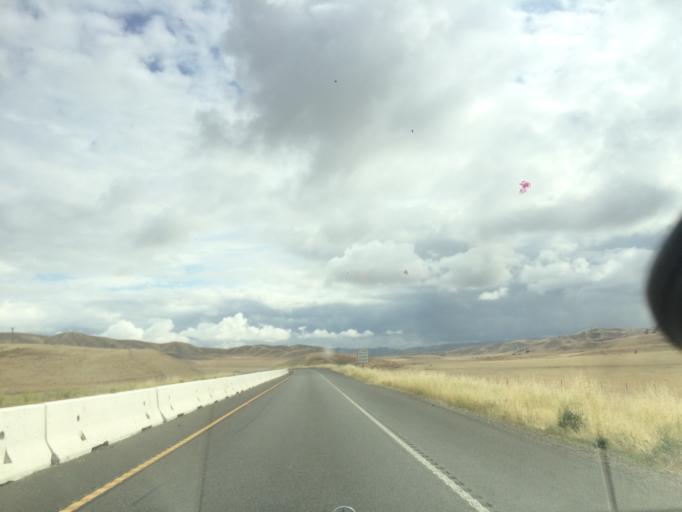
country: US
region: California
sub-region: San Luis Obispo County
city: Shandon
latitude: 35.6987
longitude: -120.3256
